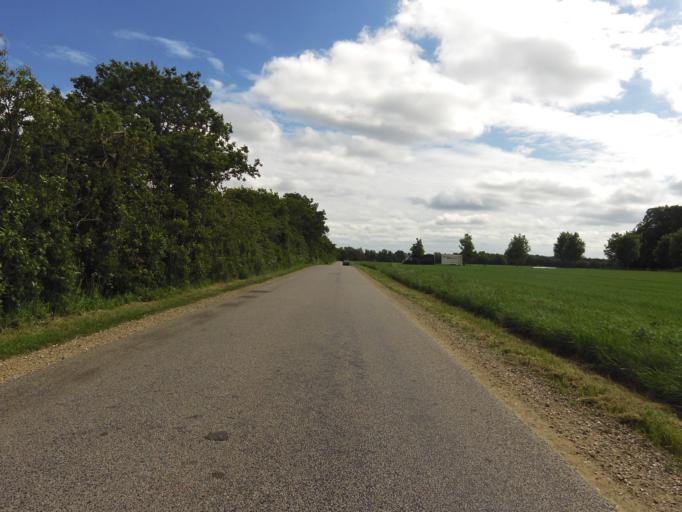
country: DK
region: South Denmark
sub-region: Vejen Kommune
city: Vejen
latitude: 55.4414
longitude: 9.1093
